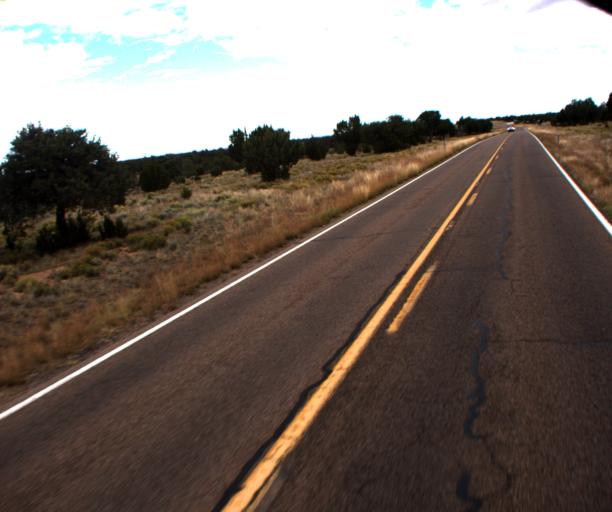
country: US
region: Arizona
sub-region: Navajo County
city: Heber-Overgaard
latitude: 34.4882
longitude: -110.4594
